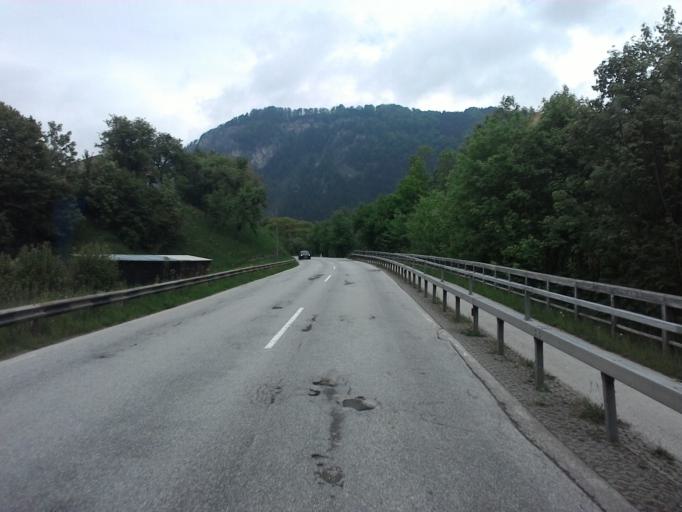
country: AT
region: Styria
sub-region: Politischer Bezirk Liezen
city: Landl
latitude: 47.6508
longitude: 14.7470
